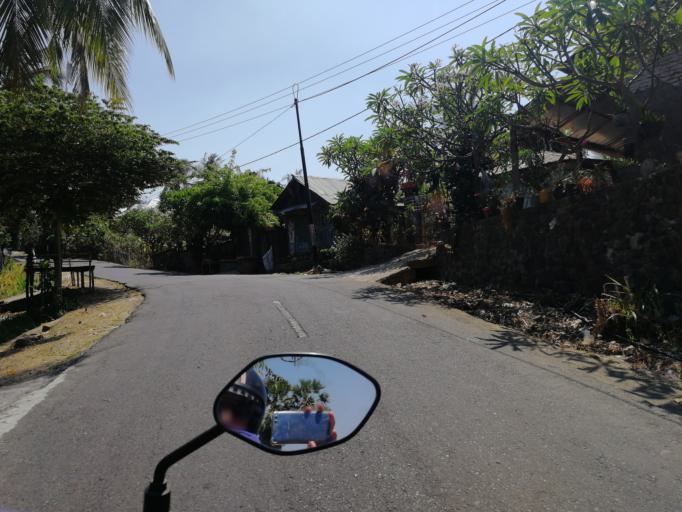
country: ID
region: Bali
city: Banjar Trunyan
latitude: -8.1330
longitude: 115.3245
